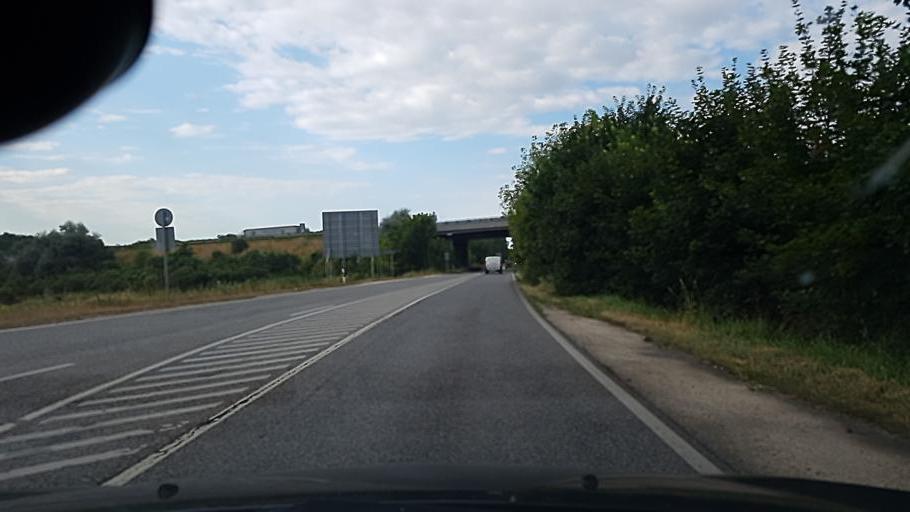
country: HU
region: Pest
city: Zsambek
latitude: 47.5083
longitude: 18.7598
